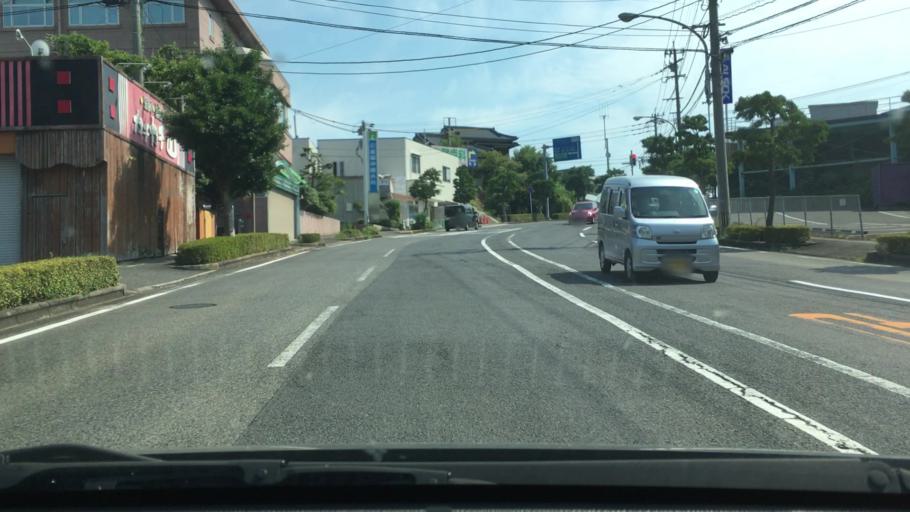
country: JP
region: Nagasaki
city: Sasebo
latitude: 33.1529
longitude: 129.7714
